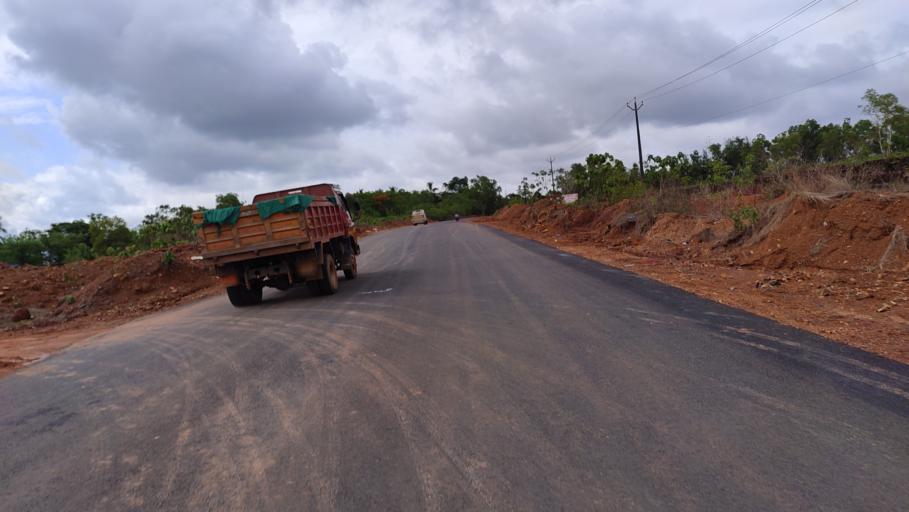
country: IN
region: Kerala
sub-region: Kasaragod District
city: Kasaragod
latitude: 12.5549
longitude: 75.0704
